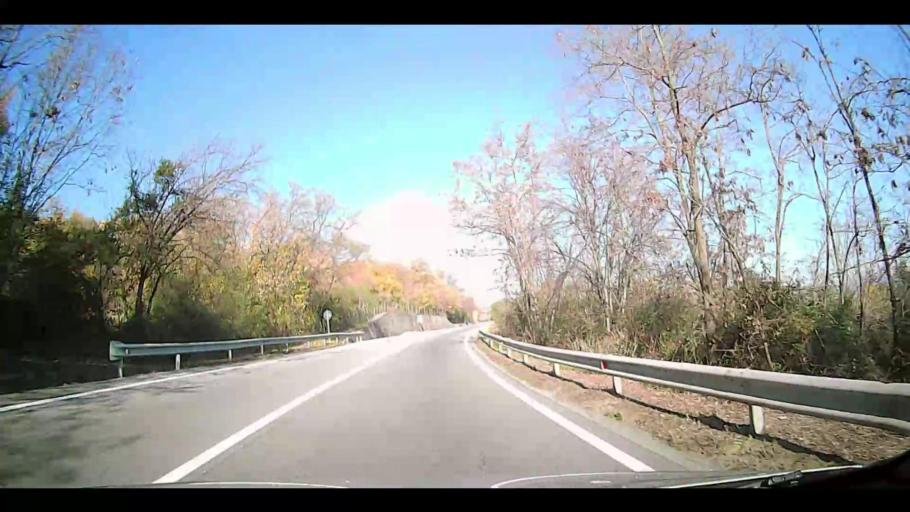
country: IT
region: Calabria
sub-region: Provincia di Crotone
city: Caccuri
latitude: 39.2043
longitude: 16.8066
